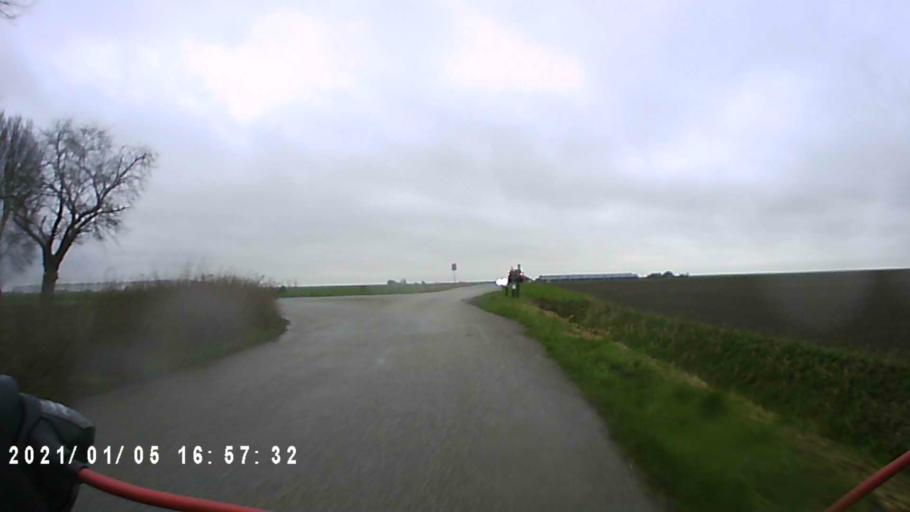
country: NL
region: Groningen
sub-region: Gemeente  Oldambt
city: Winschoten
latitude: 53.2470
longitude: 7.0563
